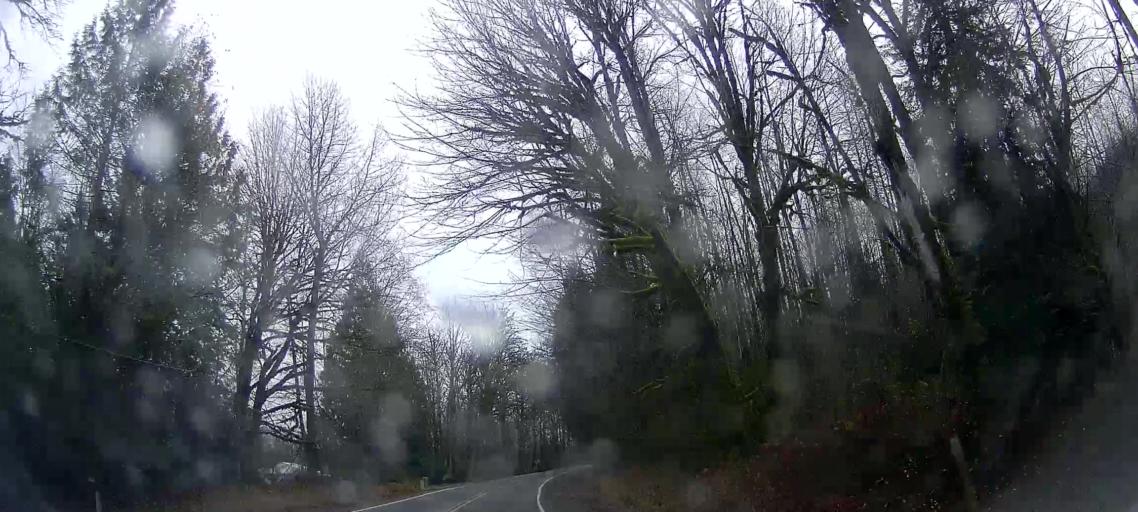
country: US
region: Washington
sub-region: Snohomish County
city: Darrington
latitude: 48.5319
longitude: -121.7914
